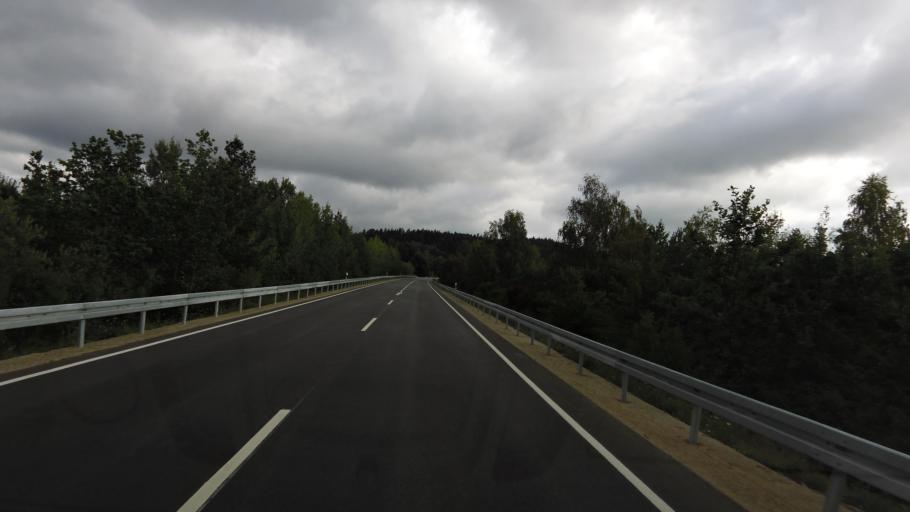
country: DE
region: Bavaria
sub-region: Lower Bavaria
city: Loitzendorf
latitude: 49.0844
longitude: 12.6400
